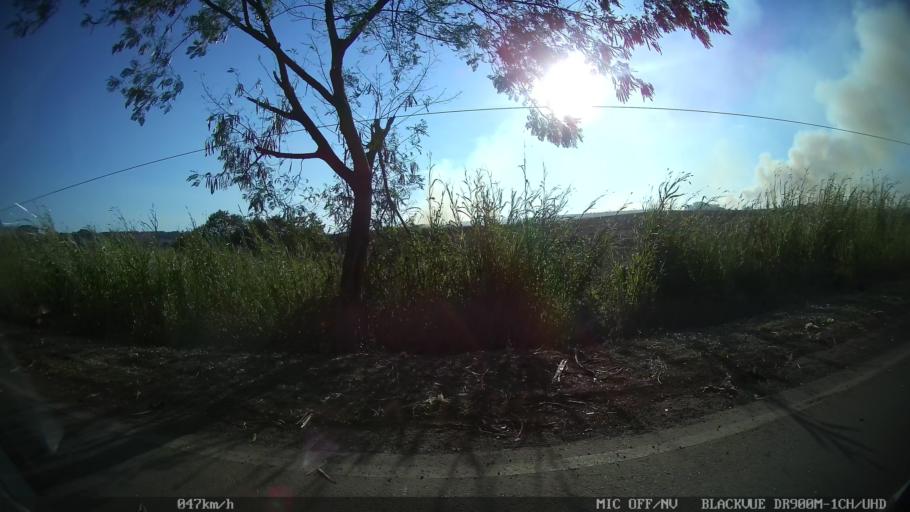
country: BR
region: Sao Paulo
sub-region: Piracicaba
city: Piracicaba
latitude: -22.6971
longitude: -47.6012
